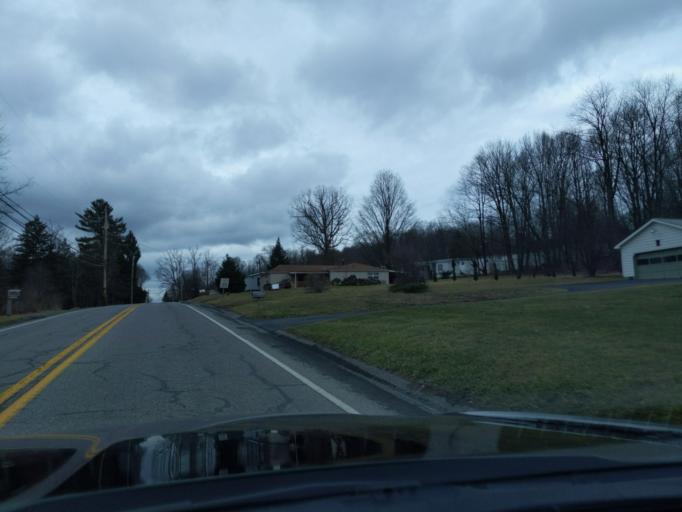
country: US
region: Pennsylvania
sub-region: Blair County
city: Bellwood
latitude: 40.5741
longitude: -78.3466
